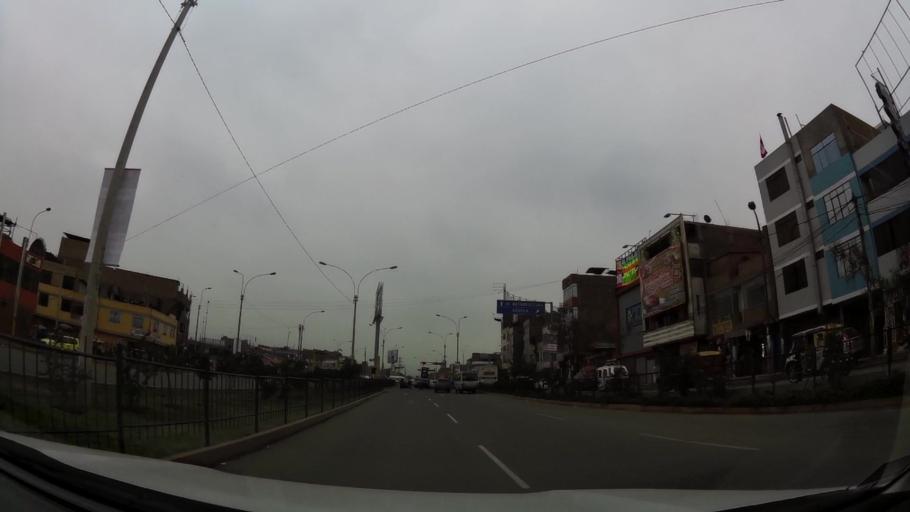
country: PE
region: Lima
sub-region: Lima
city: Vitarte
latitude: -12.0333
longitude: -76.9260
